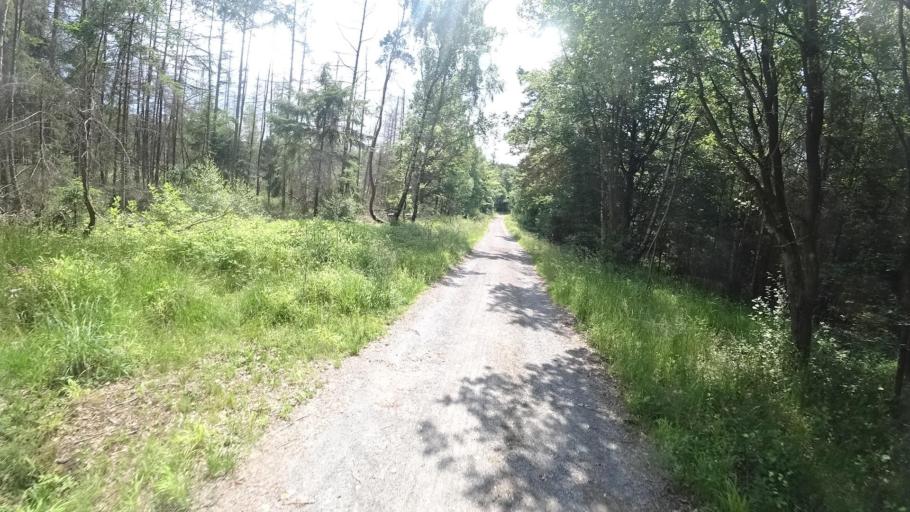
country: DE
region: Rheinland-Pfalz
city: Wolmersen
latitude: 50.7218
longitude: 7.6054
